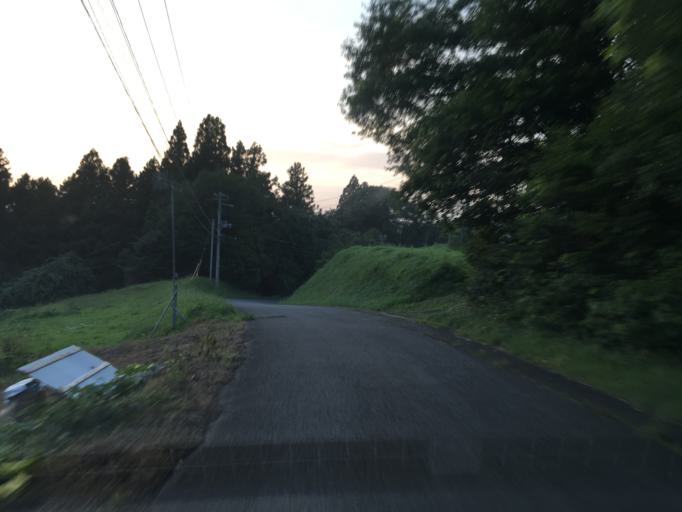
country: JP
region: Iwate
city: Ichinoseki
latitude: 38.8423
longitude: 141.2868
